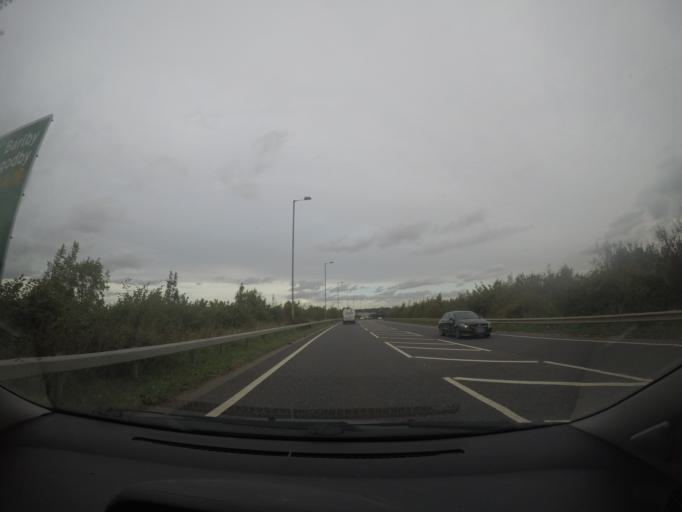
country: GB
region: England
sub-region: North Yorkshire
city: Barlby
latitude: 53.7878
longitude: -1.0392
